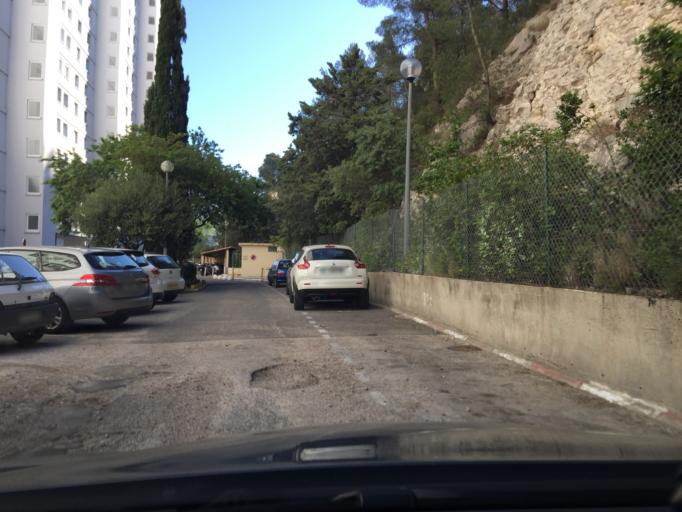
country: FR
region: Provence-Alpes-Cote d'Azur
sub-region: Departement des Bouches-du-Rhone
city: Marseille 09
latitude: 43.2508
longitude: 5.4272
